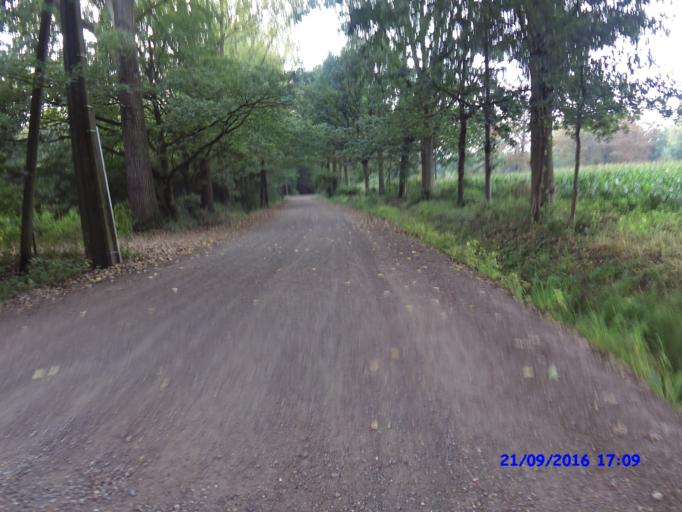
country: BE
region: Flanders
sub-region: Provincie Antwerpen
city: Schilde
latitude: 51.2298
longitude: 4.6157
